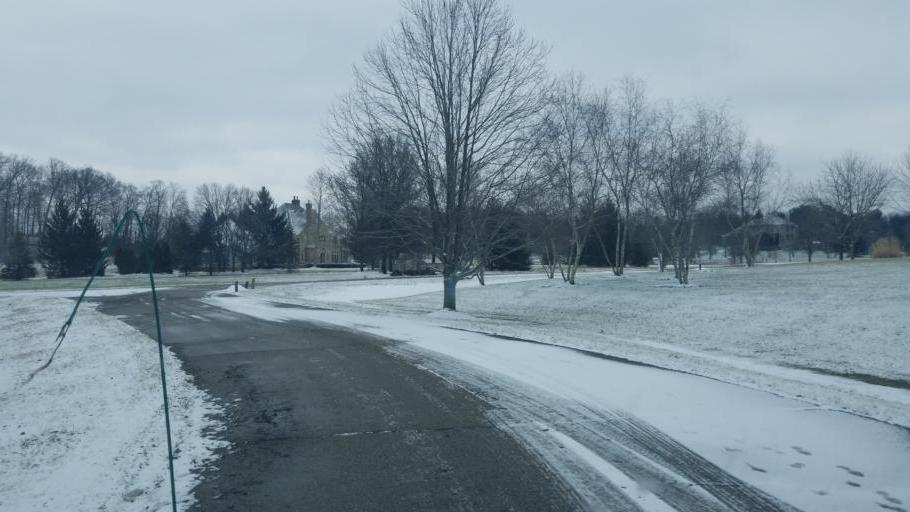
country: US
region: Ohio
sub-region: Franklin County
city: New Albany
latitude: 40.0462
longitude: -82.8405
